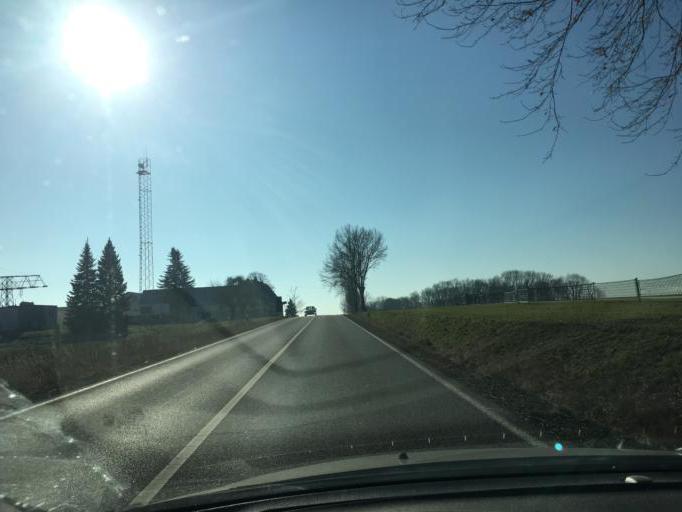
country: DE
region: Saxony
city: Penig
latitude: 50.9688
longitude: 12.6950
